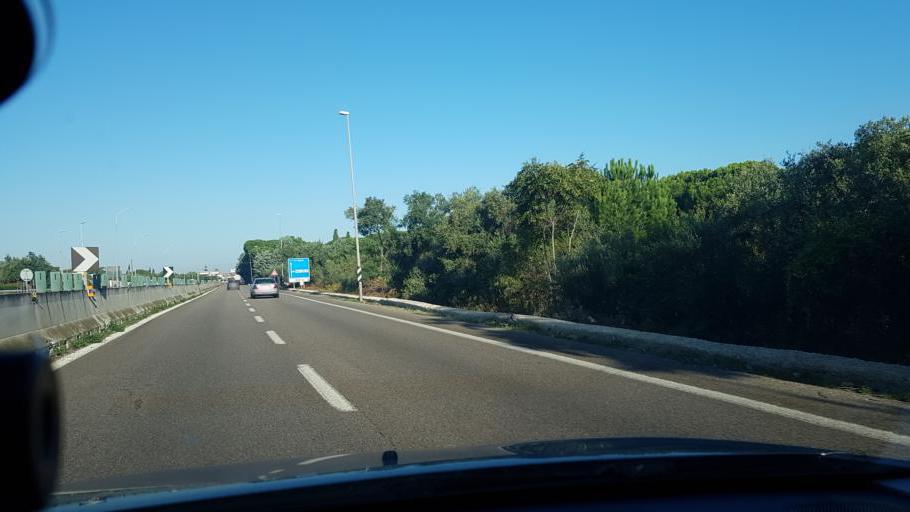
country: IT
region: Apulia
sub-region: Provincia di Bari
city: Parco Scizzo-Parchitello
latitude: 41.0848
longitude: 16.9926
